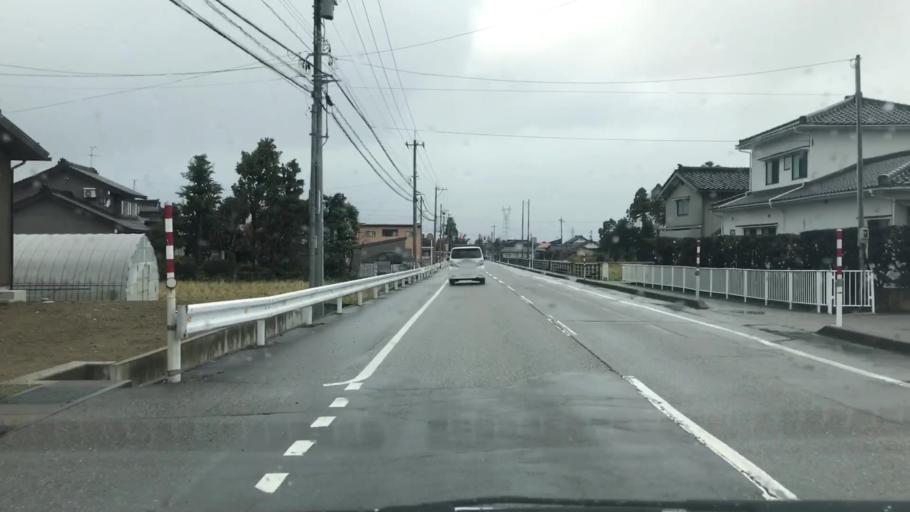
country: JP
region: Toyama
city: Kamiichi
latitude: 36.6767
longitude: 137.2904
